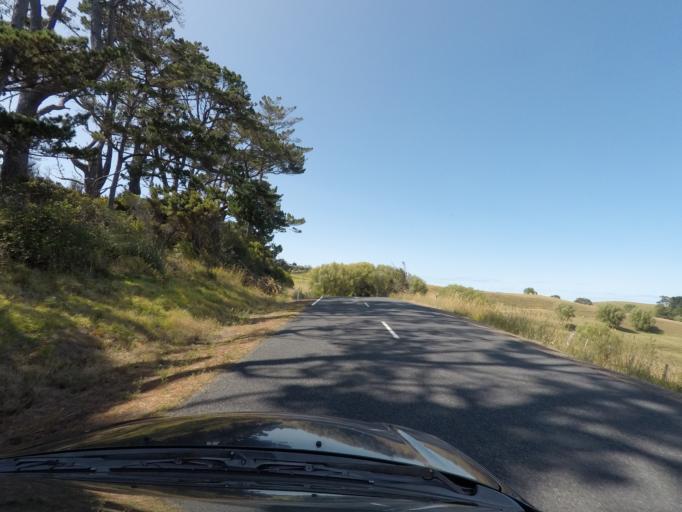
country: NZ
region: Auckland
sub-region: Auckland
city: Warkworth
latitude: -36.4493
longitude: 174.7559
